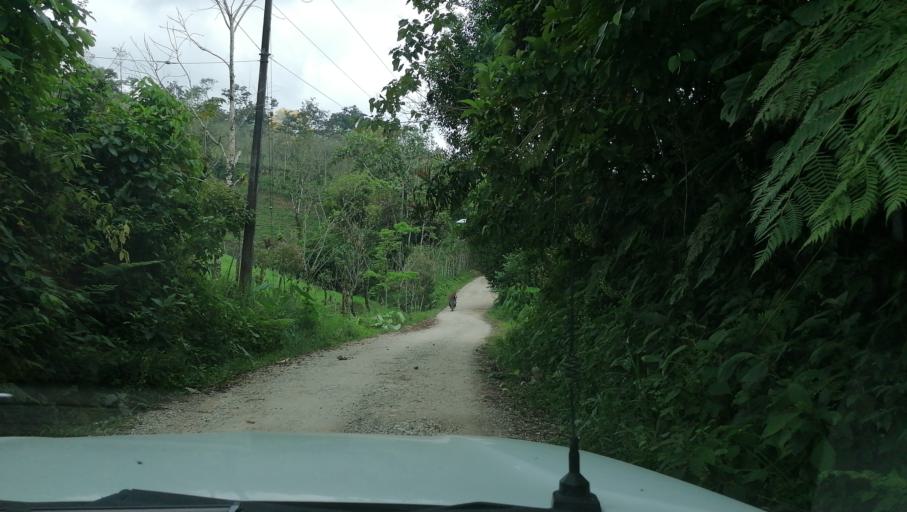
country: MX
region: Chiapas
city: Ocotepec
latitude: 17.2791
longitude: -93.2290
